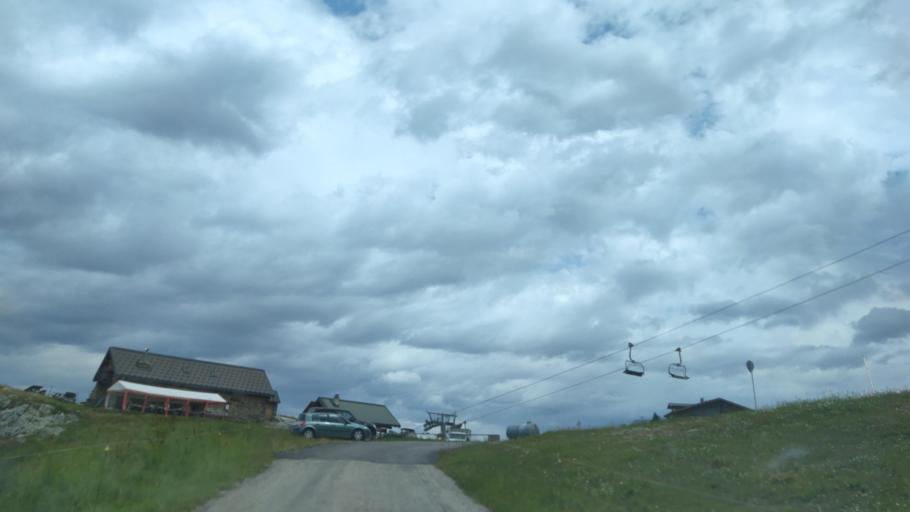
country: FR
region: Rhone-Alpes
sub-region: Departement de la Savoie
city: Courchevel
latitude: 45.3941
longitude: 6.6554
